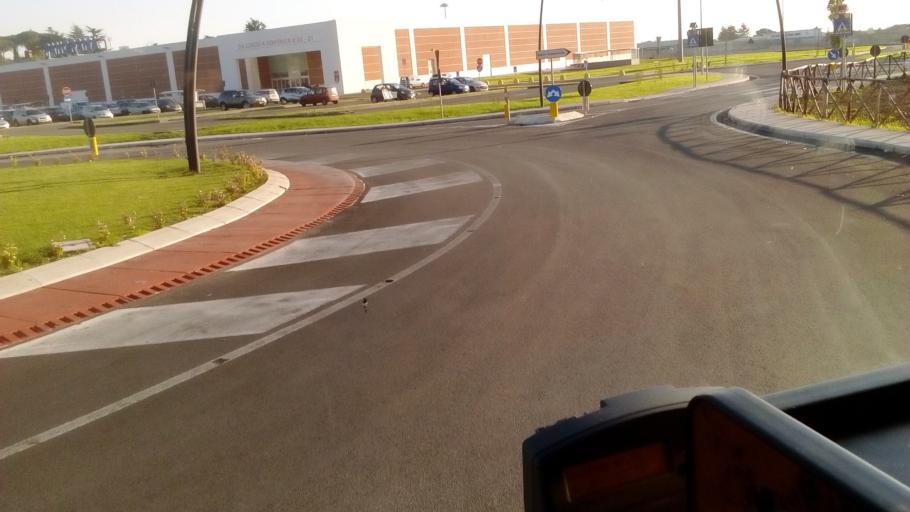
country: IT
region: Latium
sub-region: Citta metropolitana di Roma Capitale
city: Pavona
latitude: 41.7182
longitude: 12.6233
